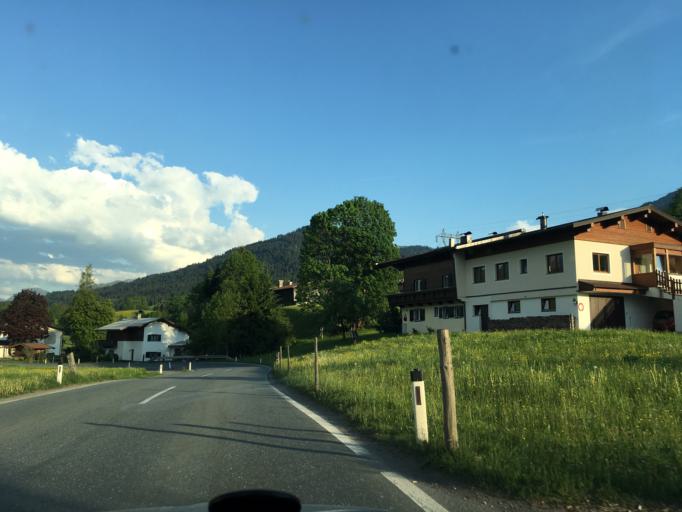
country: AT
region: Tyrol
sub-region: Politischer Bezirk Kitzbuhel
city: Sankt Johann in Tirol
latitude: 47.5124
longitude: 12.4562
